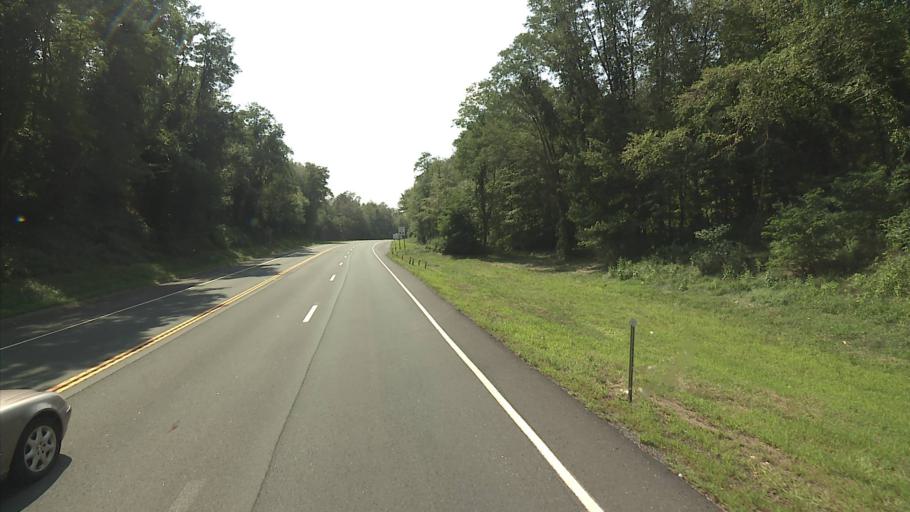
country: US
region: Connecticut
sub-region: Middlesex County
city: East Haddam
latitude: 41.4431
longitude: -72.4726
